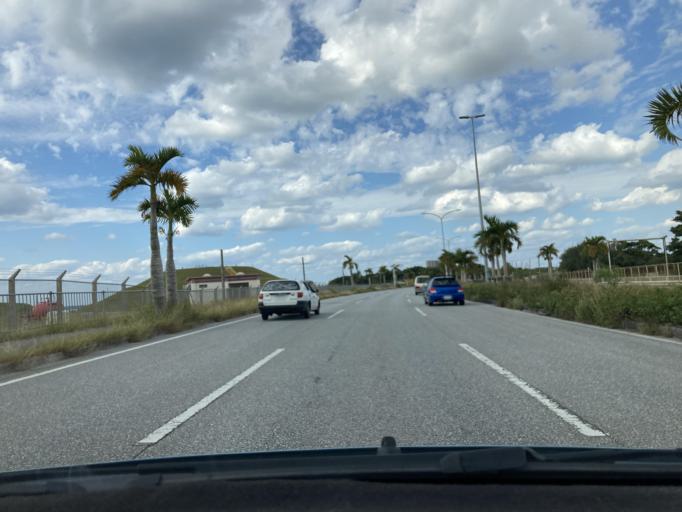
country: JP
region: Okinawa
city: Chatan
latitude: 26.3453
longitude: 127.7475
